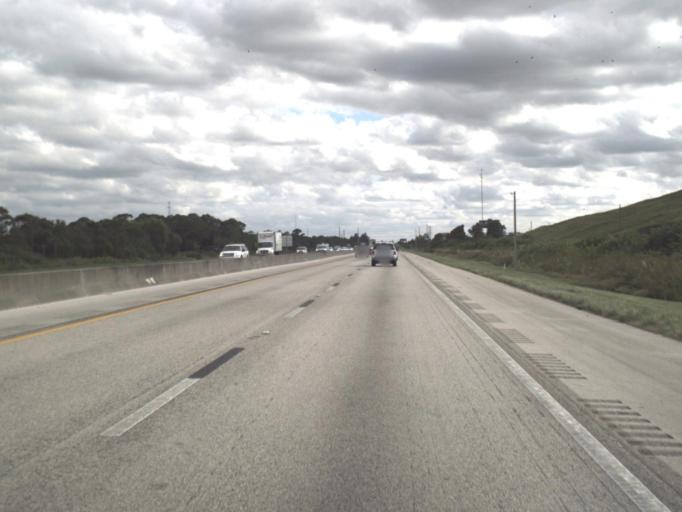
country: US
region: Florida
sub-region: Saint Lucie County
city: Fort Pierce South
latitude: 27.3927
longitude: -80.3930
